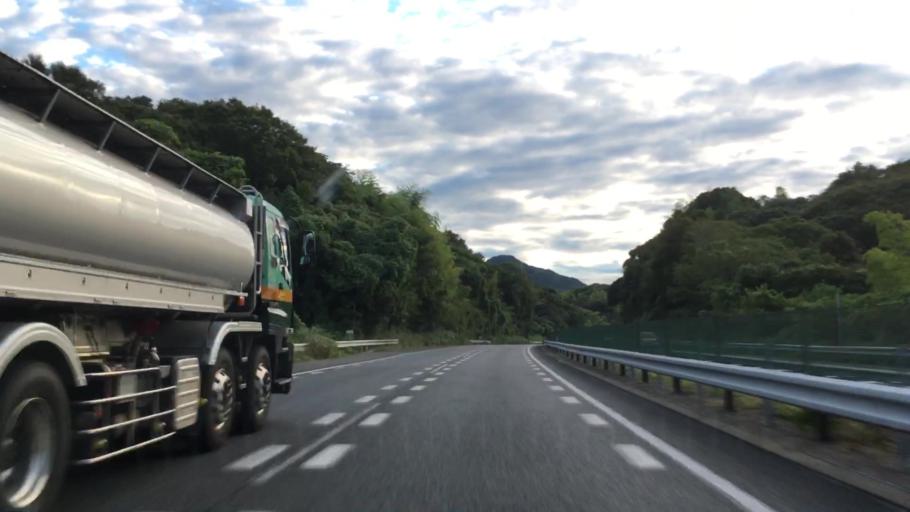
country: JP
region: Yamaguchi
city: Shimonoseki
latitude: 34.0468
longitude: 130.9998
